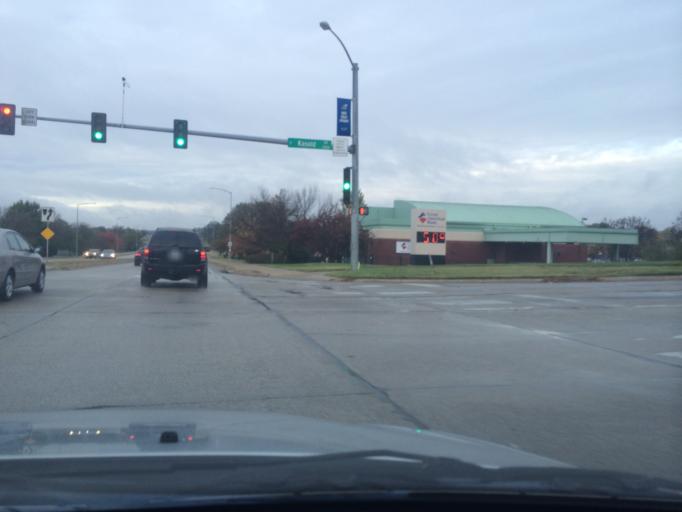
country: US
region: Kansas
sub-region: Douglas County
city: Lawrence
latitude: 38.9427
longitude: -95.2793
